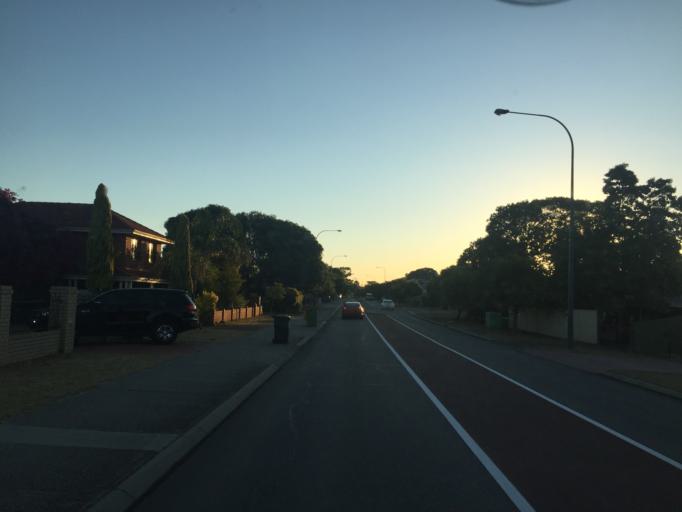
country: AU
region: Western Australia
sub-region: Belmont
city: Rivervale
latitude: -31.9590
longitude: 115.9172
